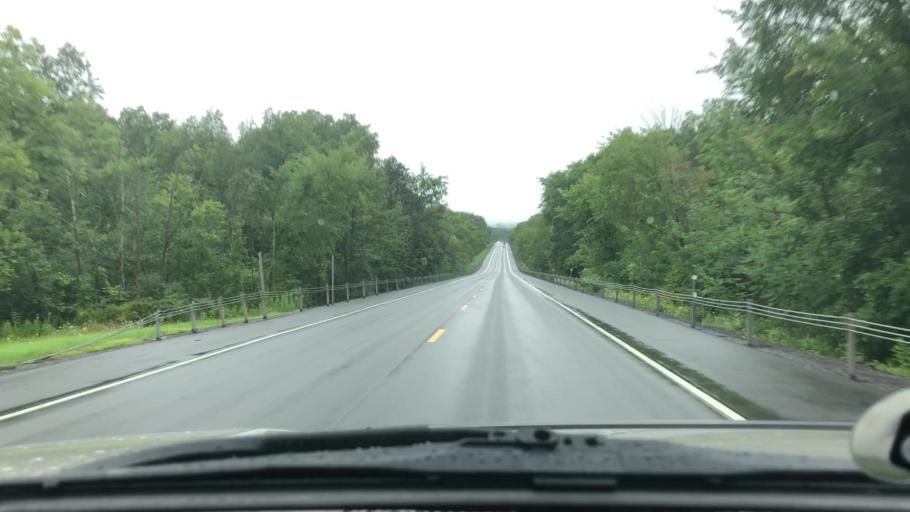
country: US
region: New York
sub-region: Greene County
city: Cairo
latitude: 42.3100
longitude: -74.0577
